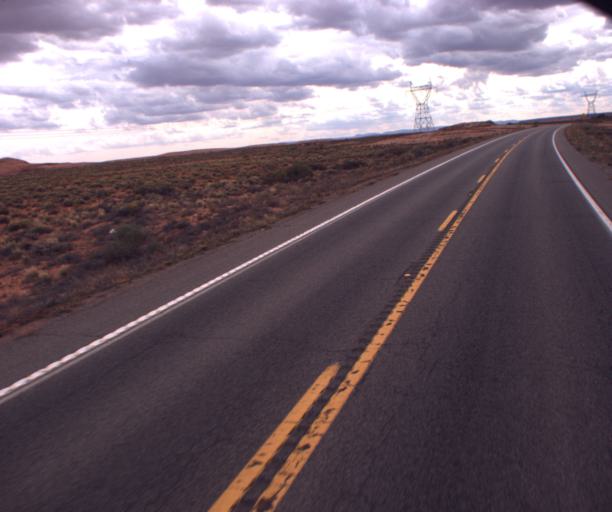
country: US
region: Arizona
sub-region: Navajo County
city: Kayenta
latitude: 36.8513
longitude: -109.8317
